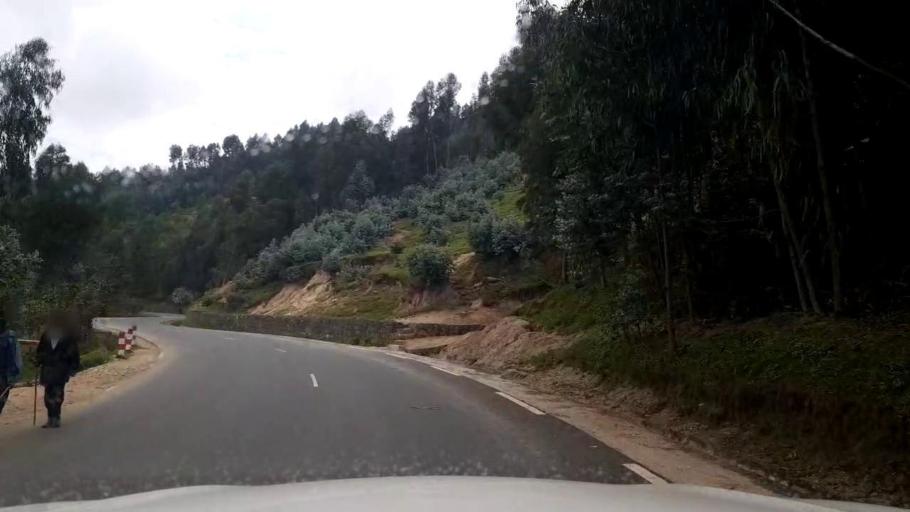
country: RW
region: Northern Province
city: Musanze
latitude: -1.6636
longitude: 29.5128
